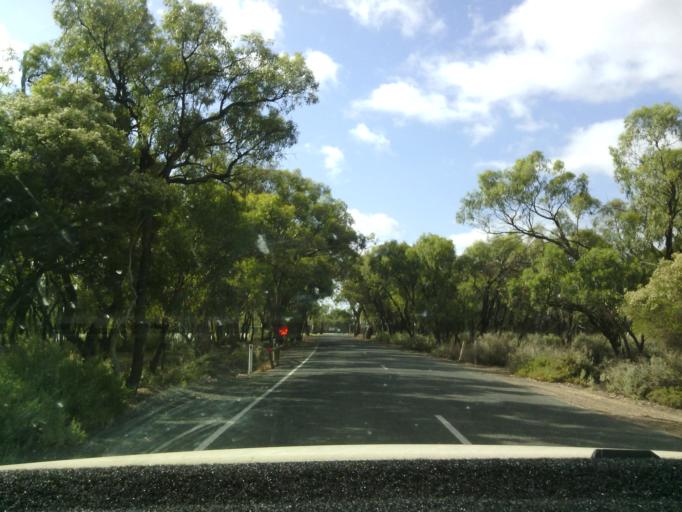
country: AU
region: South Australia
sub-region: Berri and Barmera
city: Berri
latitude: -34.2851
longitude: 140.6307
